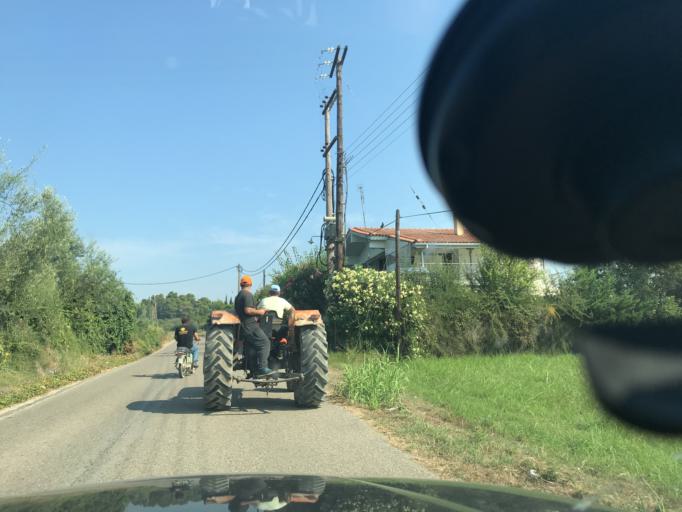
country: GR
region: West Greece
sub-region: Nomos Ileias
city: Kardamas
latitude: 37.7198
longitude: 21.3680
